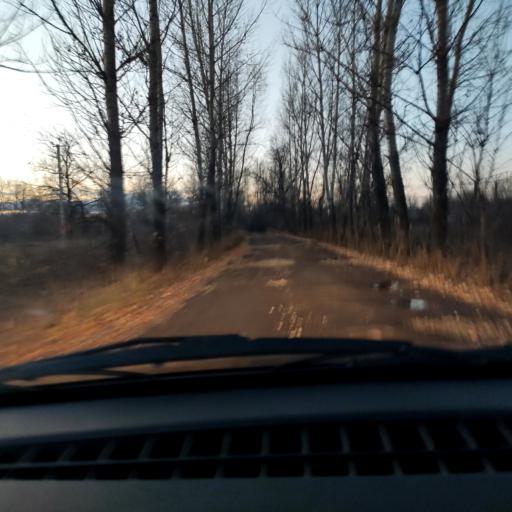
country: RU
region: Bashkortostan
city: Ufa
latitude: 54.6539
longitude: 55.8897
